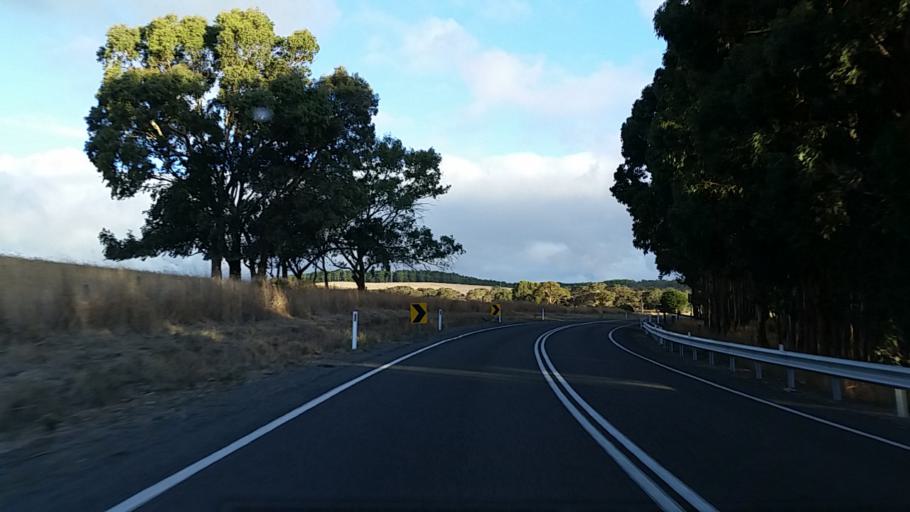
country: AU
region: South Australia
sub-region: Yankalilla
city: Normanville
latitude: -35.5613
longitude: 138.2003
